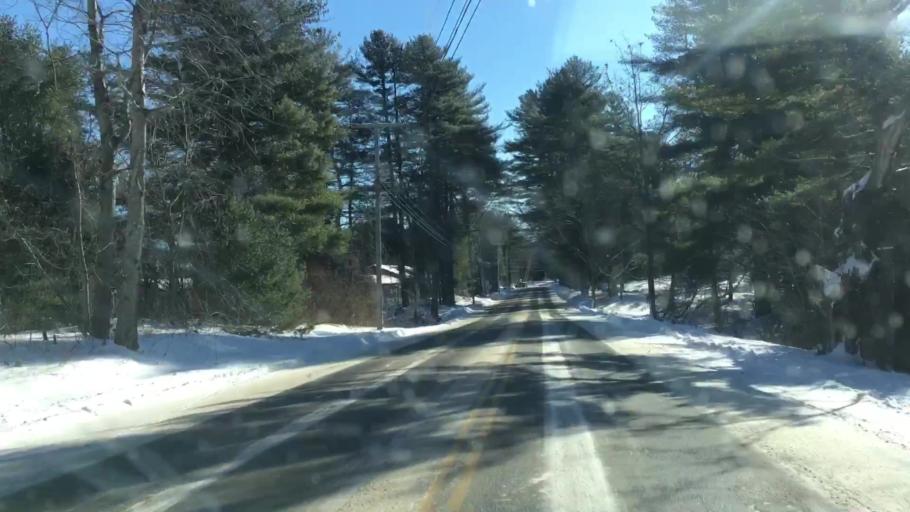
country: US
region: Maine
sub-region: Sagadahoc County
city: Topsham
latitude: 43.9042
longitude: -70.0004
